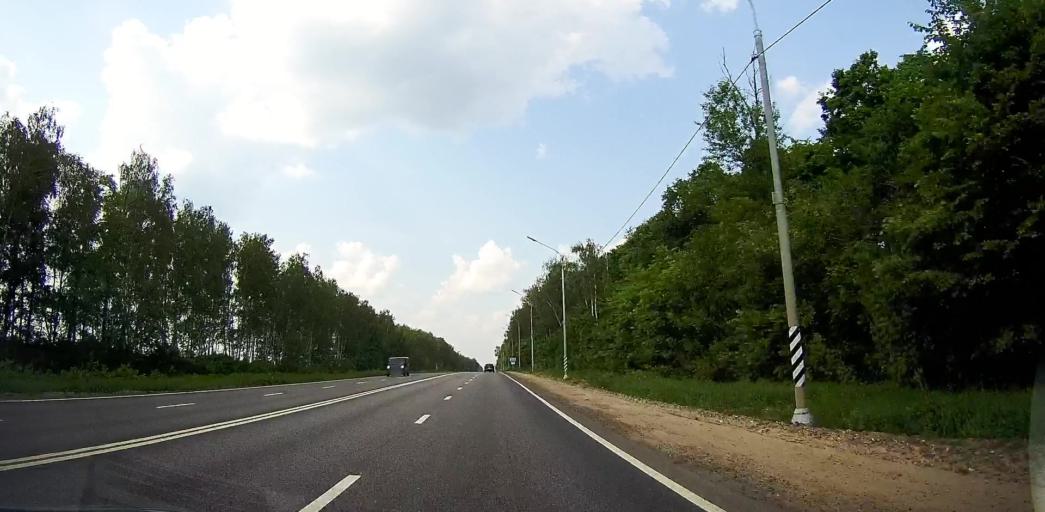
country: RU
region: Moskovskaya
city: Mikhnevo
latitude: 55.0968
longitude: 37.9504
